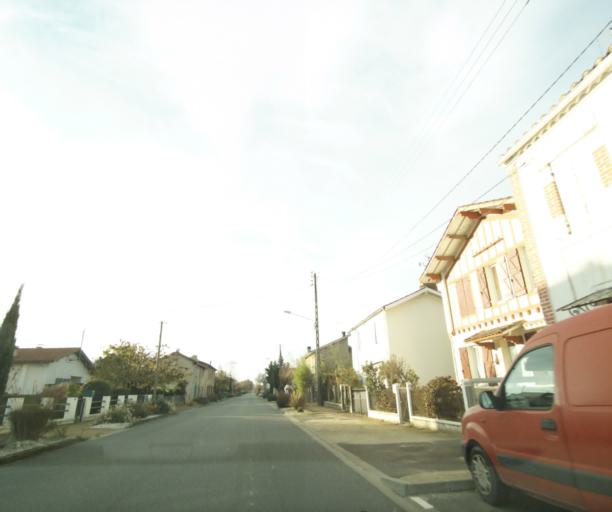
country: FR
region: Aquitaine
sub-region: Departement des Landes
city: Gabarret
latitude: 43.9870
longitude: 0.0059
